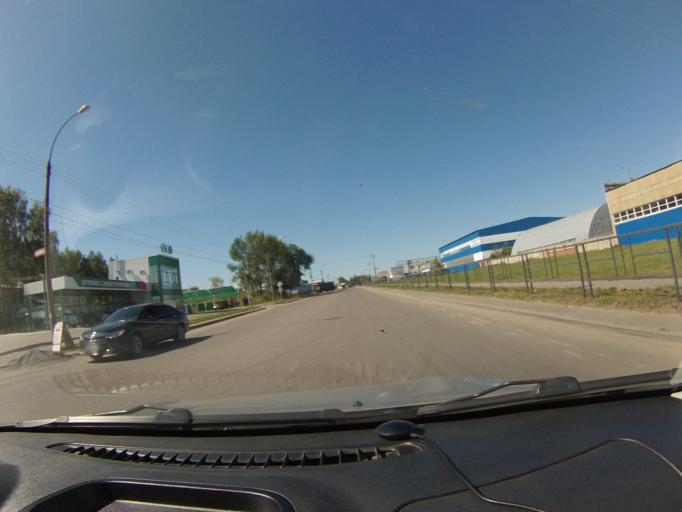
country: RU
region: Tambov
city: Donskoye
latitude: 52.7581
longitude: 41.4635
